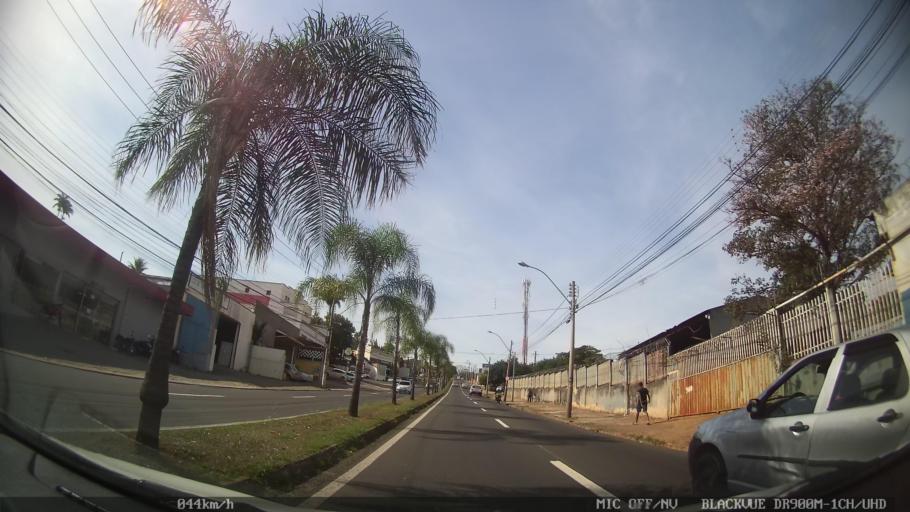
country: BR
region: Sao Paulo
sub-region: Piracicaba
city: Piracicaba
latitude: -22.7324
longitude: -47.6622
